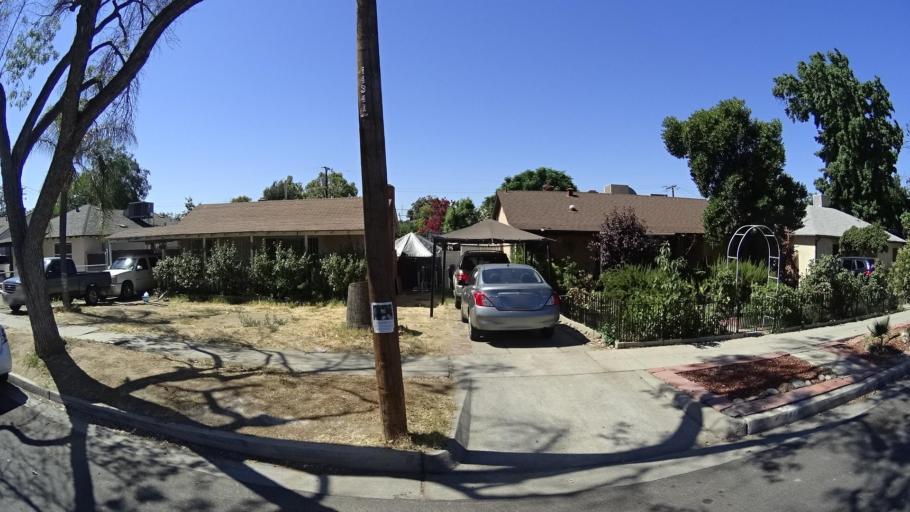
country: US
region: California
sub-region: Fresno County
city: Fresno
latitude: 36.7768
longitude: -119.7892
